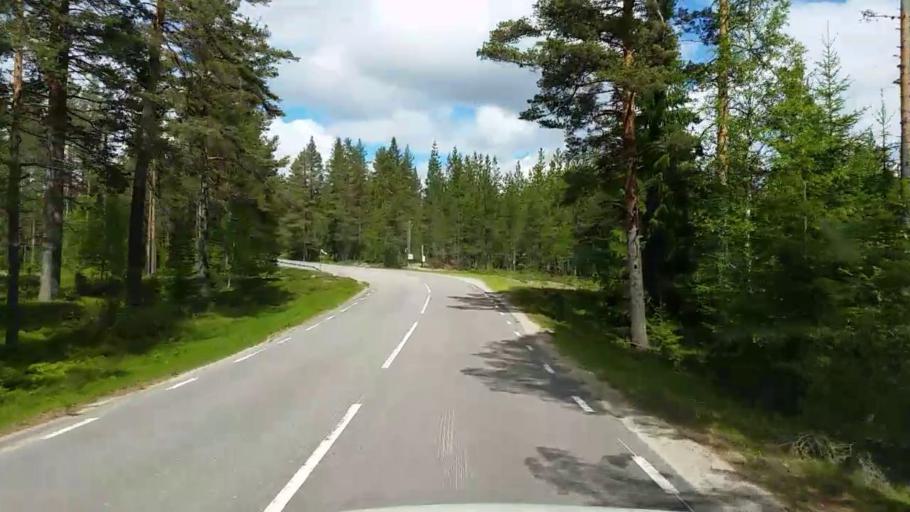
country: SE
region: Gaevleborg
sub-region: Bollnas Kommun
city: Vittsjo
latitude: 61.1314
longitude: 16.1764
